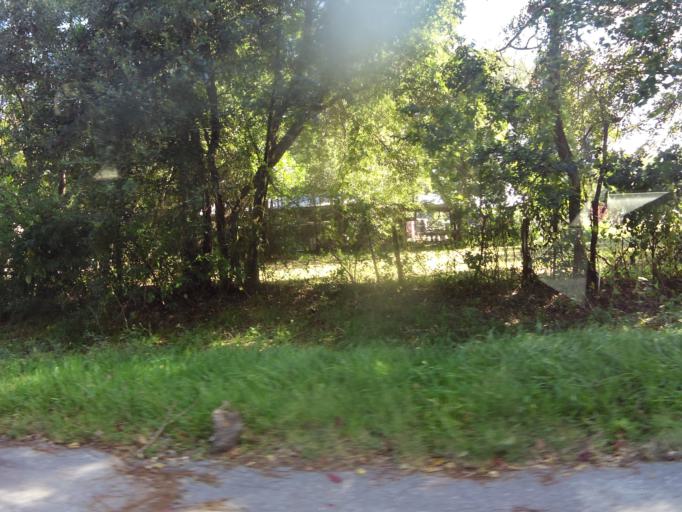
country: US
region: Florida
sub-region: Duval County
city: Jacksonville
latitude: 30.2733
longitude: -81.6340
